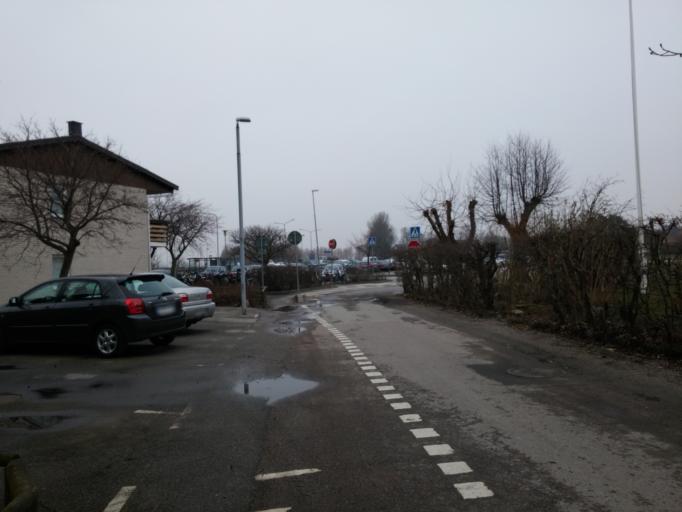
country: SE
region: Skane
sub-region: Vellinge Kommun
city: Hollviken
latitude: 55.4231
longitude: 12.9599
